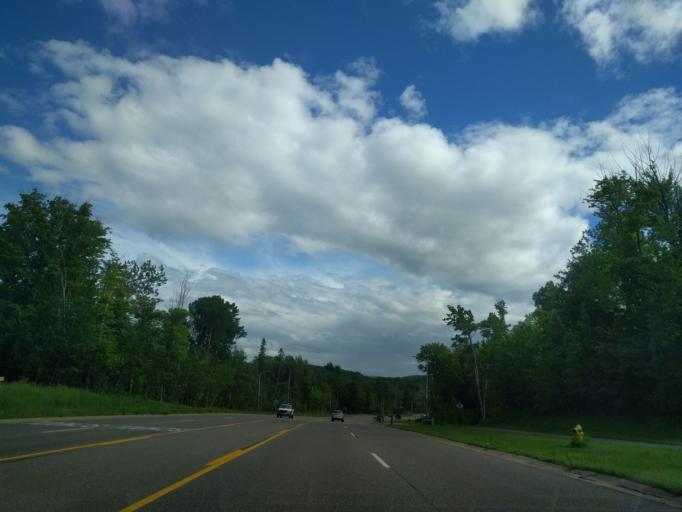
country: US
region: Michigan
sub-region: Marquette County
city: Marquette
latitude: 46.5304
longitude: -87.4176
